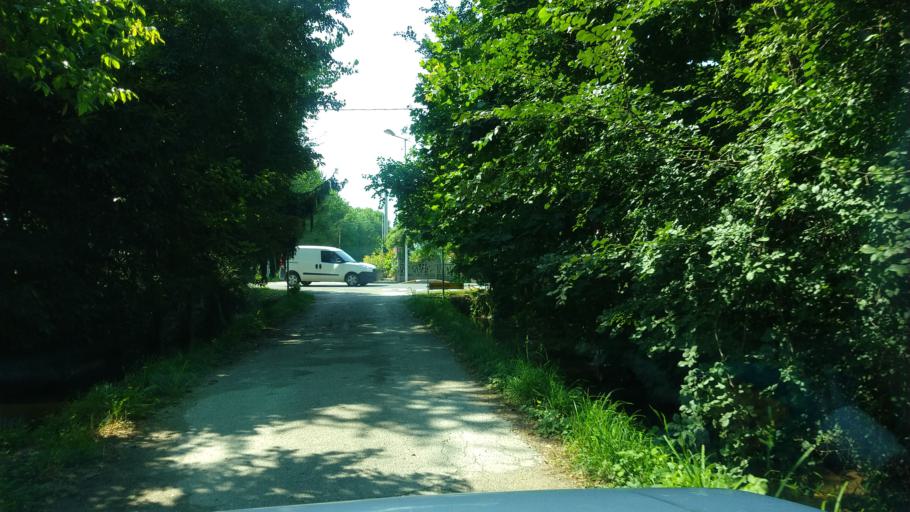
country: IT
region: Veneto
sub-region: Provincia di Vicenza
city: Pozzoleone
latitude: 45.6767
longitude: 11.6764
